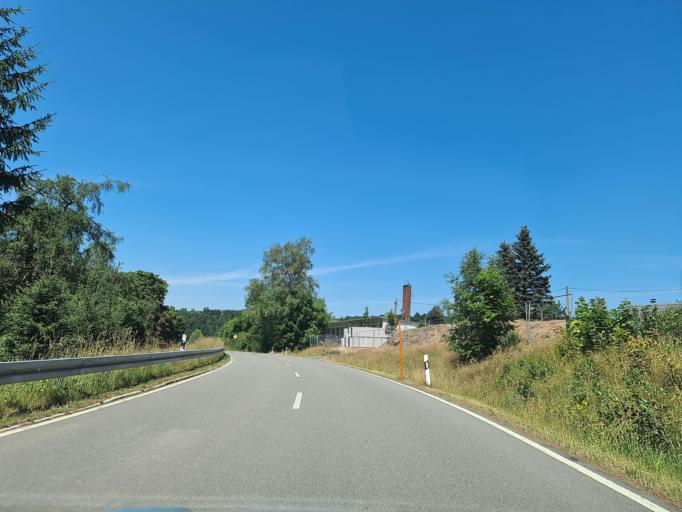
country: DE
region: Saxony
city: Rechenberg-Bienenmuhle
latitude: 50.6991
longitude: 13.5209
